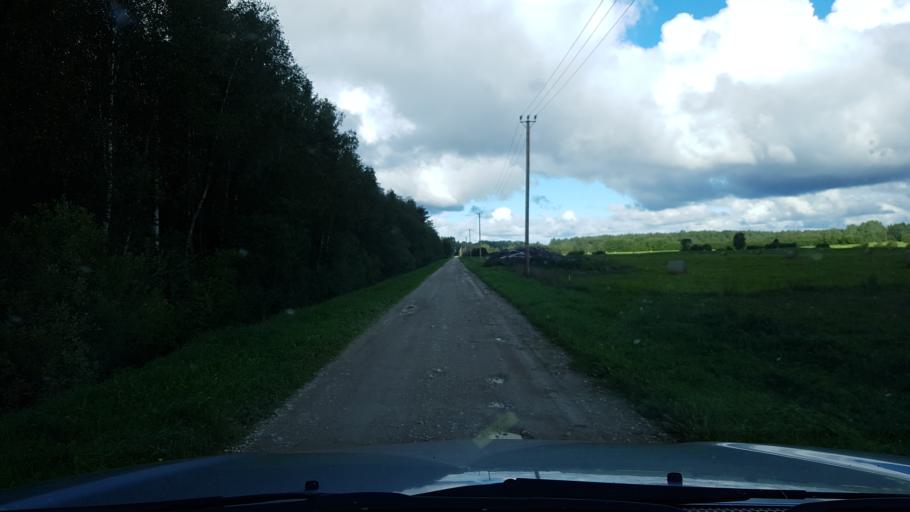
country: EE
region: Harju
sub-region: Rae vald
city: Vaida
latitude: 59.2485
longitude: 25.0739
